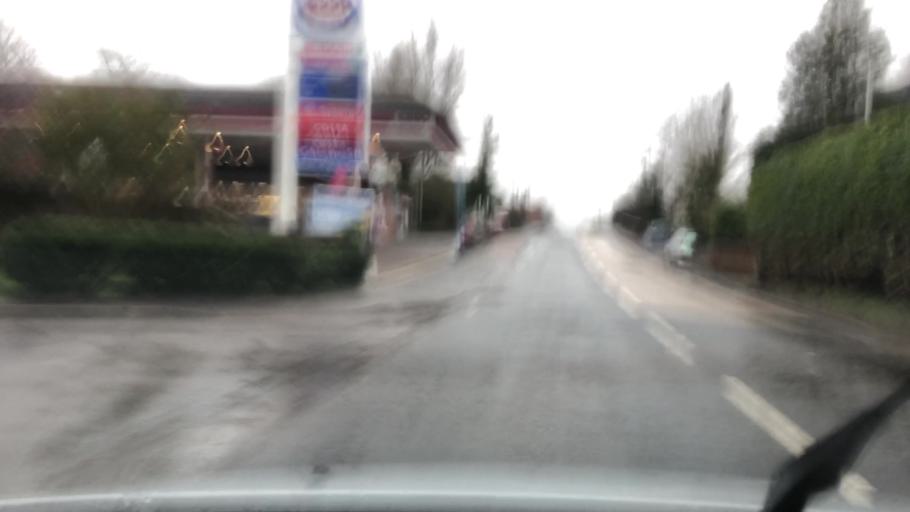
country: GB
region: England
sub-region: Hampshire
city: Odiham
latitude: 51.2606
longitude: -0.9519
